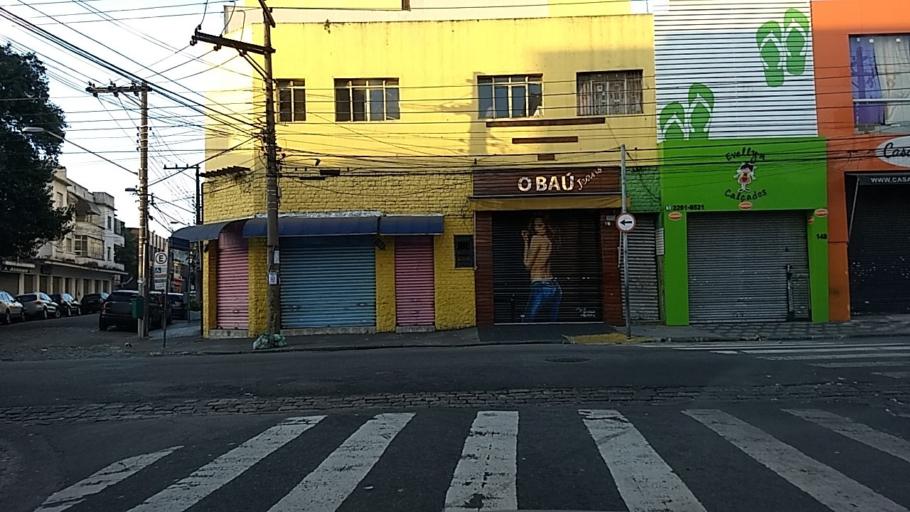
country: BR
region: Sao Paulo
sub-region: Sao Paulo
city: Sao Paulo
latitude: -23.5405
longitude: -46.6153
